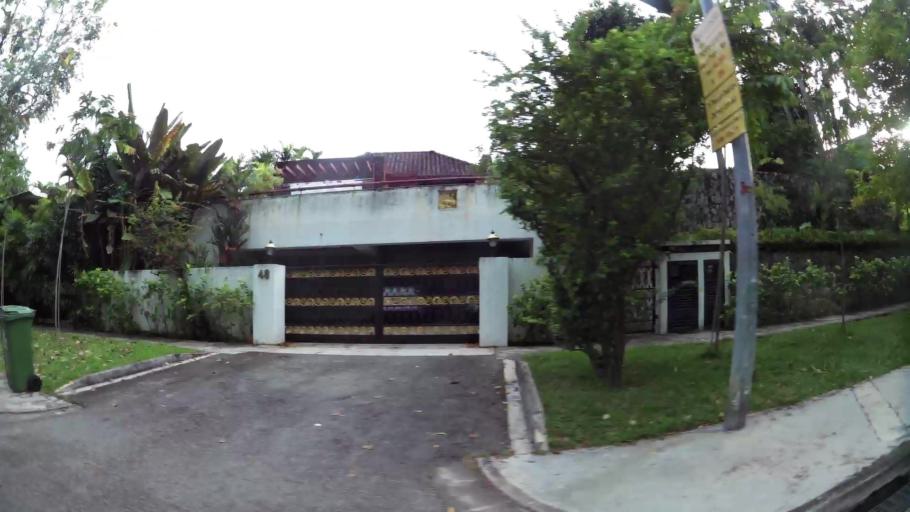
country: SG
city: Singapore
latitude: 1.3222
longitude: 103.8401
